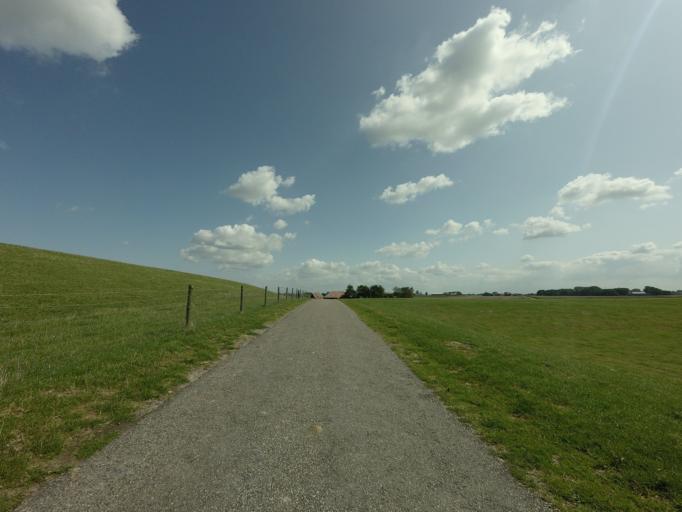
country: NL
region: Friesland
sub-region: Gemeente Ferwerderadiel
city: Hallum
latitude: 53.3195
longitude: 5.7543
